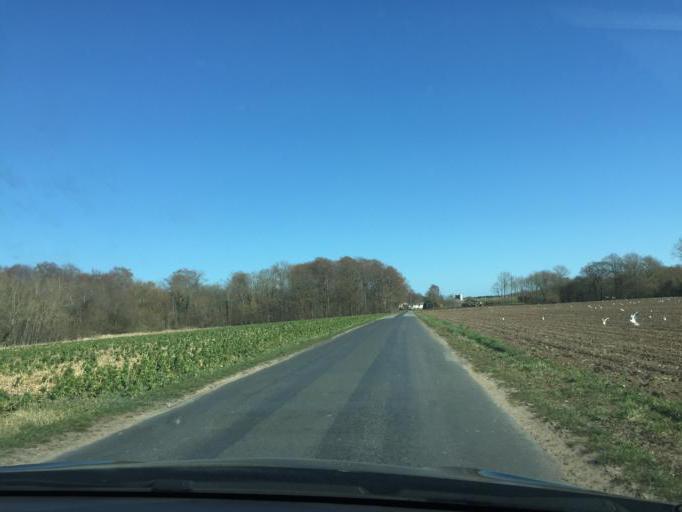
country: DK
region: South Denmark
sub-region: Kerteminde Kommune
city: Langeskov
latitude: 55.3414
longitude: 10.5613
